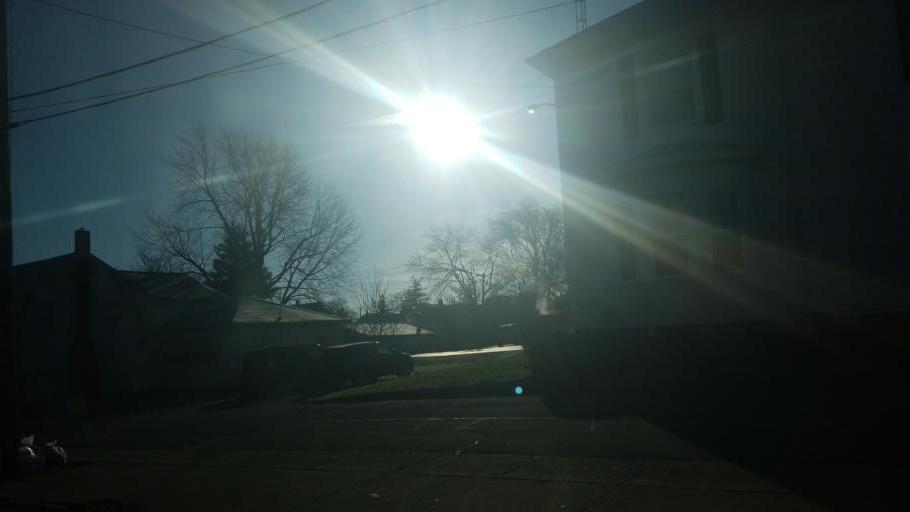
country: US
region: Ohio
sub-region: Marion County
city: Marion
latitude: 40.5802
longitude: -83.1264
